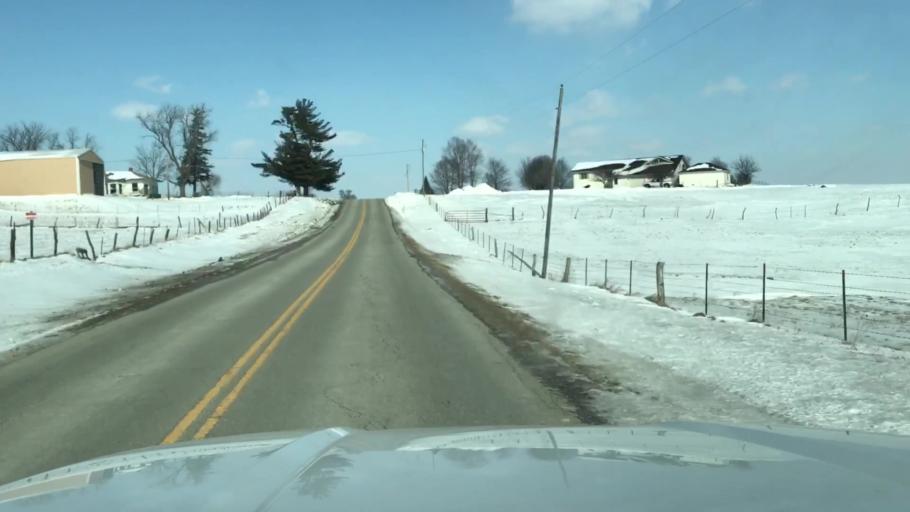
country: US
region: Missouri
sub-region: Nodaway County
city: Maryville
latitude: 40.3811
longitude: -94.7215
